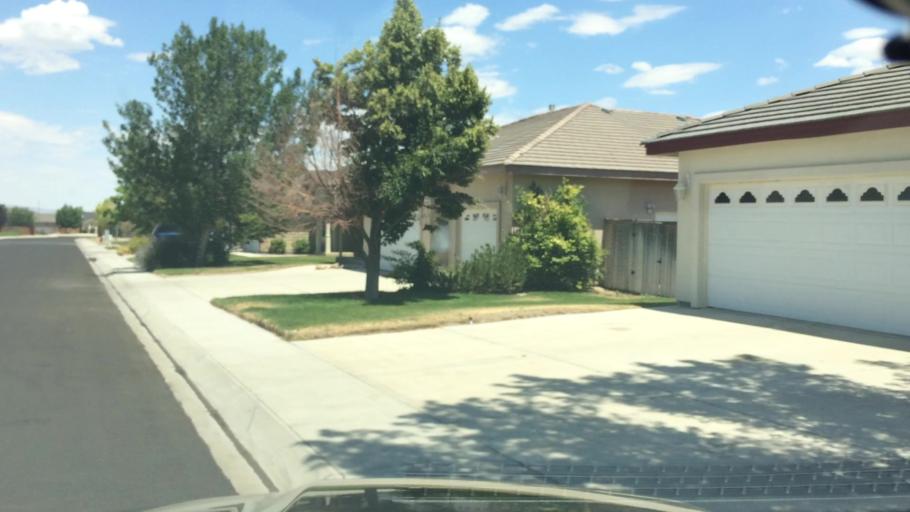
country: US
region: Nevada
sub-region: Lyon County
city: Fernley
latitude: 39.5876
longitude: -119.1408
